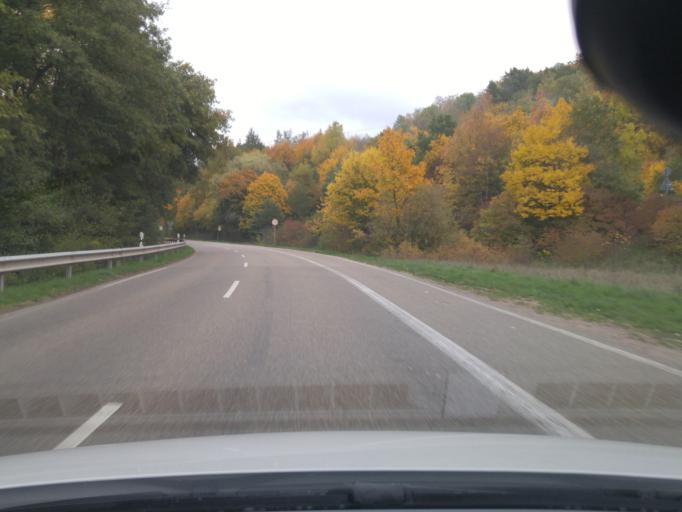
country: DE
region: Rheinland-Pfalz
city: Albersweiler
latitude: 49.2181
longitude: 8.0069
